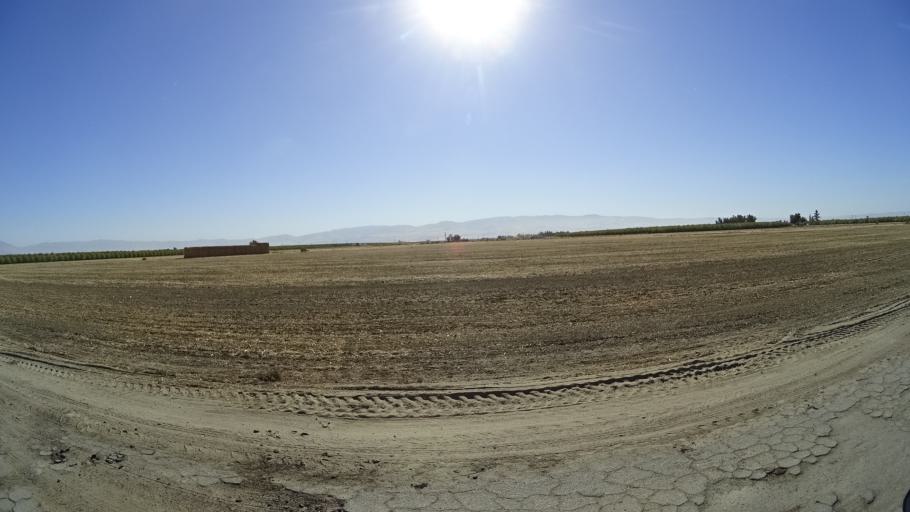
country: US
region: California
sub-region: Kern County
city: Greenfield
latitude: 35.2599
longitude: -119.0677
